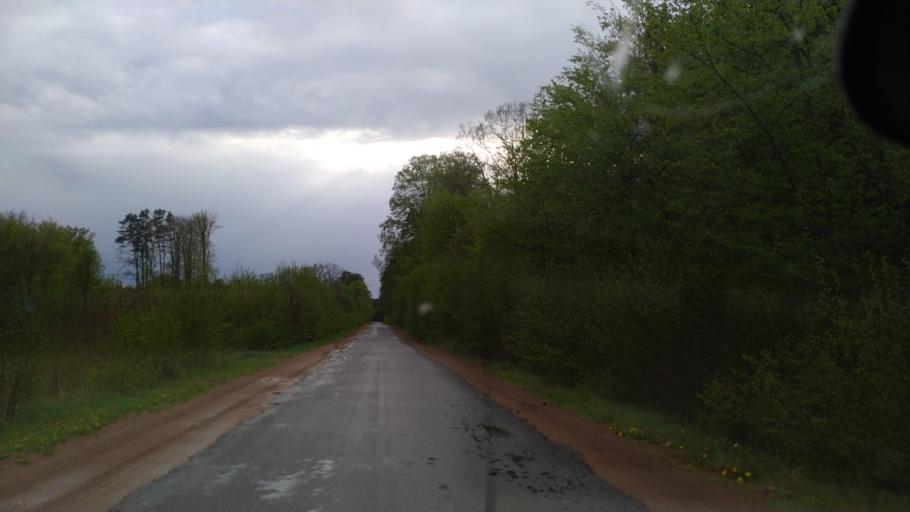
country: PL
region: Pomeranian Voivodeship
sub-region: Powiat starogardzki
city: Osiek
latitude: 53.7084
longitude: 18.5825
